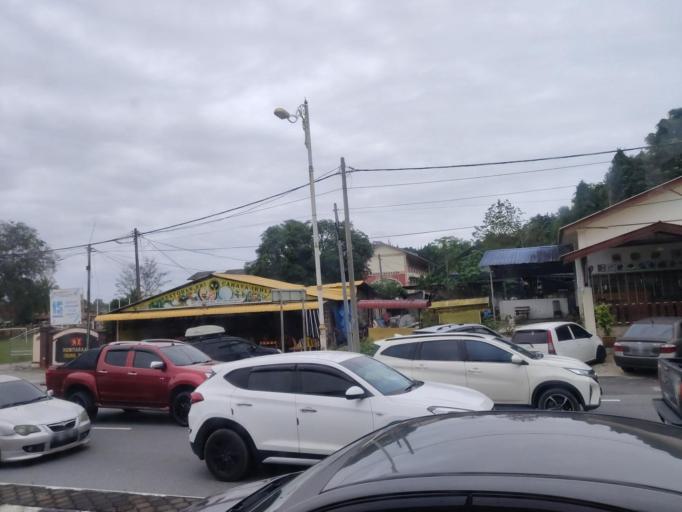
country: MY
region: Terengganu
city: Kuala Terengganu
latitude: 5.3144
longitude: 103.1433
